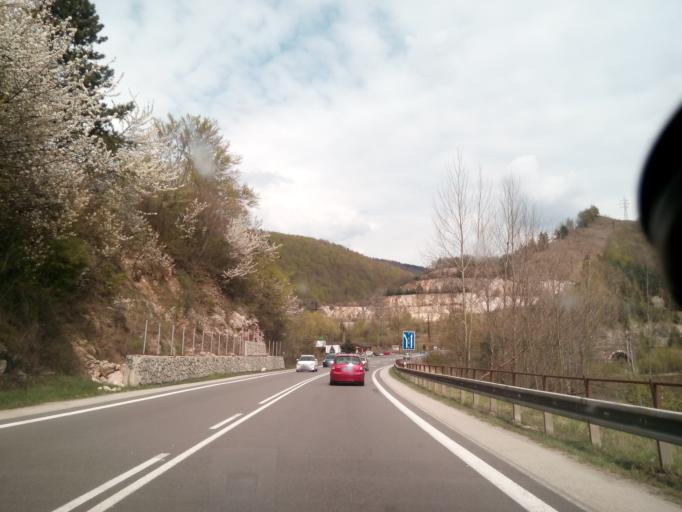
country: SK
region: Zilinsky
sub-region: Okres Zilina
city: Terchova
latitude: 49.1501
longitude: 19.0949
